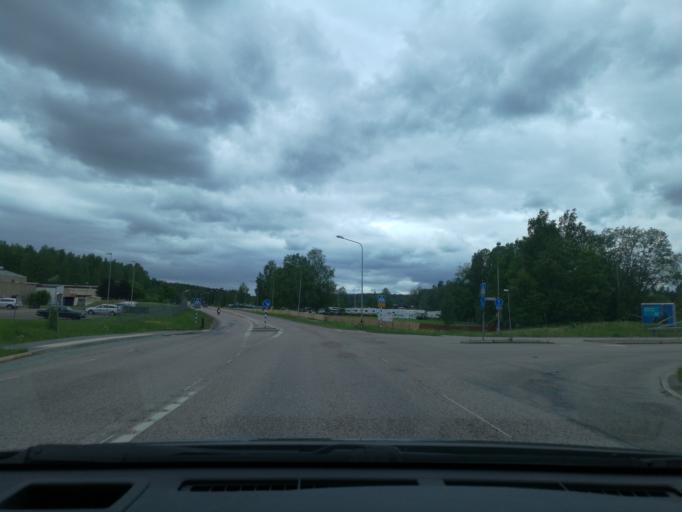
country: SE
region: Vaestmanland
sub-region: Fagersta Kommun
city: Fagersta
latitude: 59.9817
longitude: 15.7988
